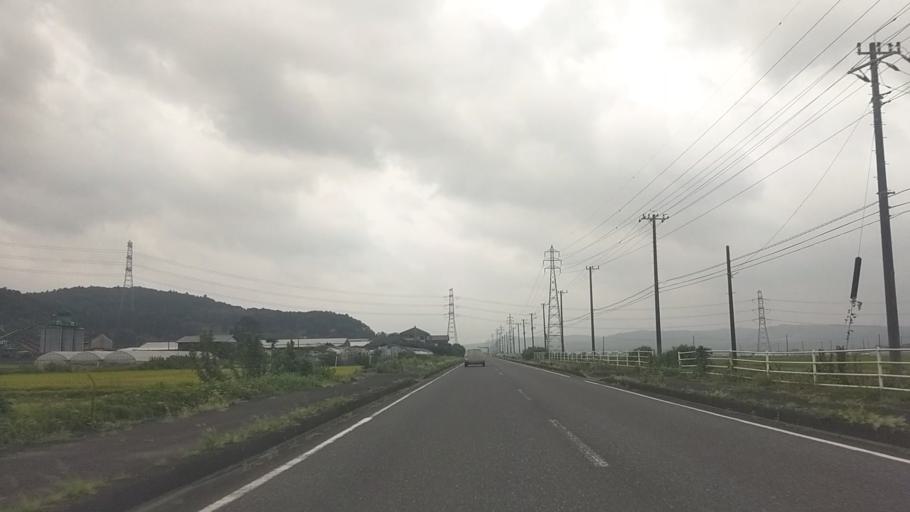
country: JP
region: Chiba
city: Kisarazu
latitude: 35.3497
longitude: 140.0548
